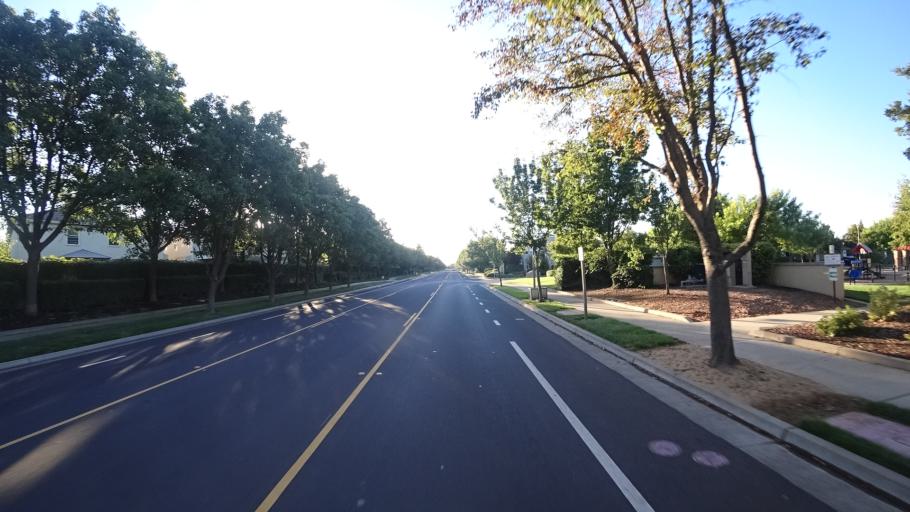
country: US
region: California
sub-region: Sacramento County
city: Laguna
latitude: 38.4029
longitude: -121.4719
